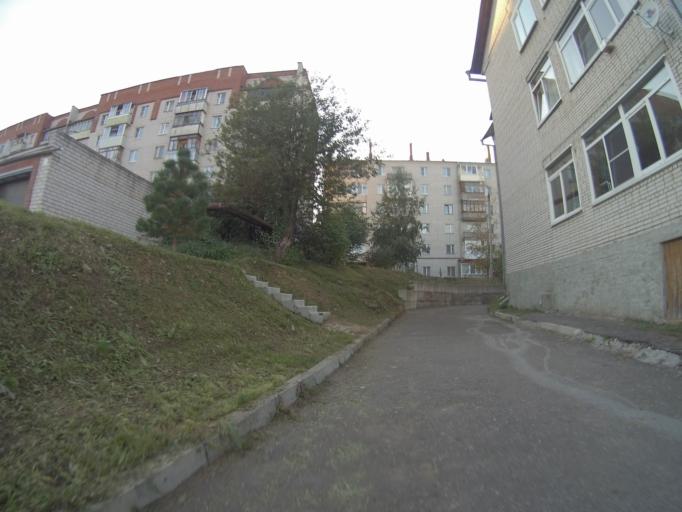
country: RU
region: Vladimir
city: Vladimir
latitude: 56.1107
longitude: 40.3780
